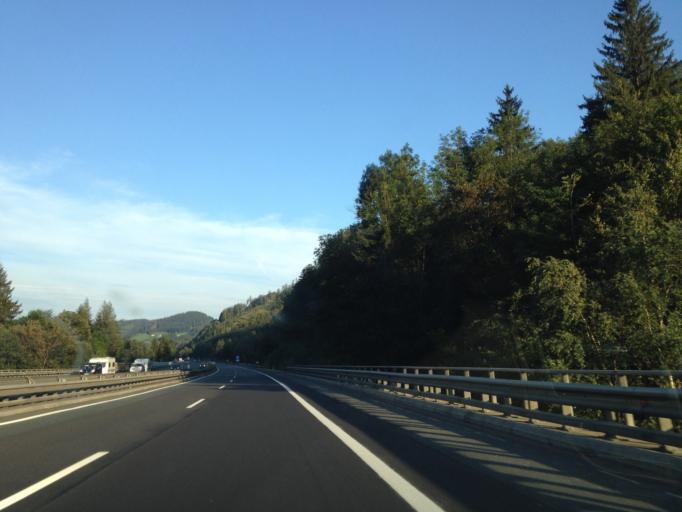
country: AT
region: Styria
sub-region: Politischer Bezirk Graz-Umgebung
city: Ubelbach
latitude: 47.2295
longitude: 15.2176
